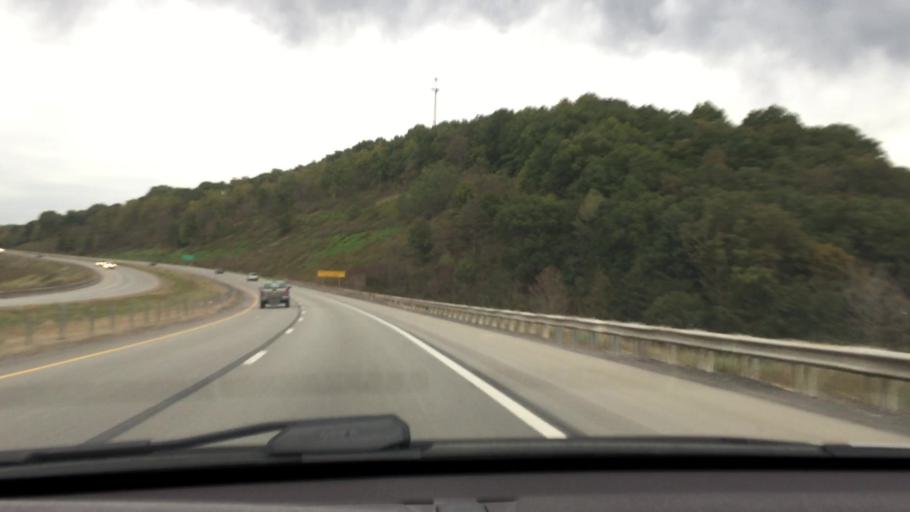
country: US
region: Pennsylvania
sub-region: Beaver County
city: West Mayfield
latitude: 40.7459
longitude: -80.3660
